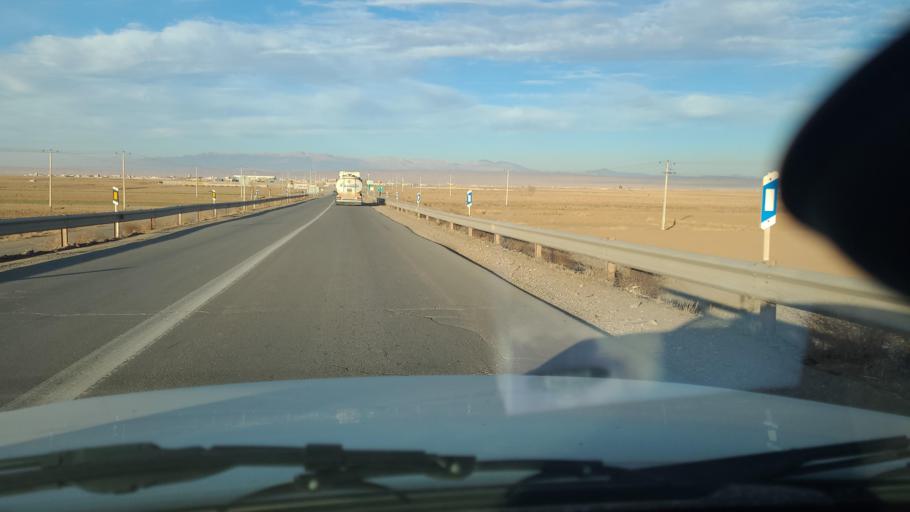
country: IR
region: Razavi Khorasan
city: Neqab
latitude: 36.6054
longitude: 57.5915
